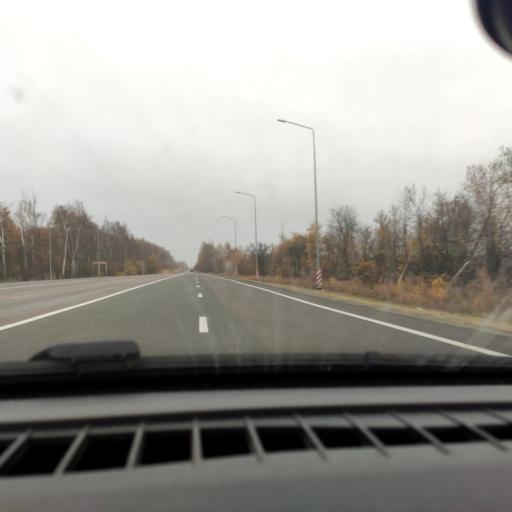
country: RU
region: Voronezj
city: Kolodeznyy
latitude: 51.3440
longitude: 39.0239
